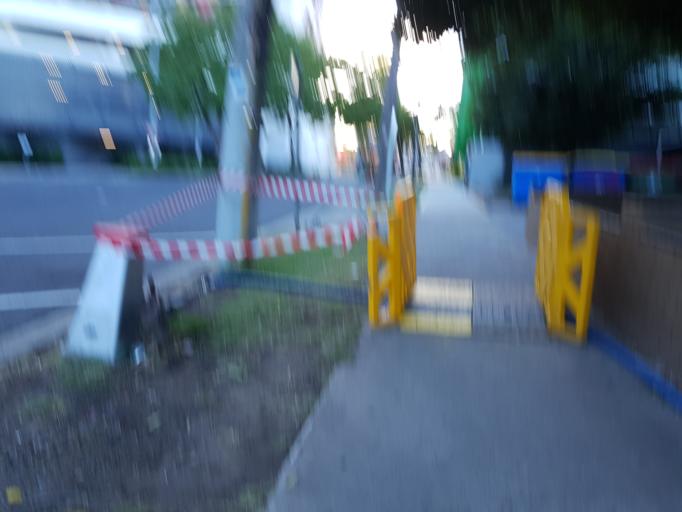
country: AU
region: Victoria
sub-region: Maribyrnong
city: Footscray
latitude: -37.8017
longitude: 144.8964
